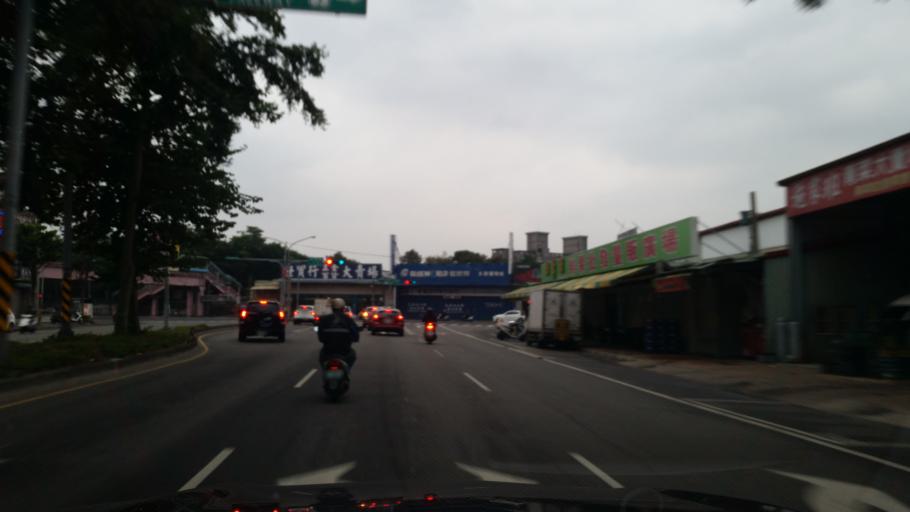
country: TW
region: Taiwan
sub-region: Taoyuan
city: Taoyuan
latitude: 25.0540
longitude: 121.3594
